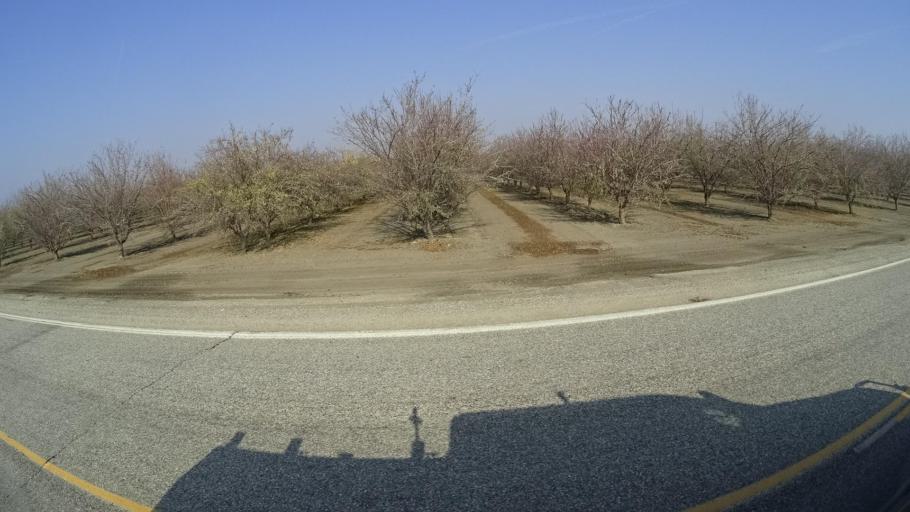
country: US
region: California
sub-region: Kern County
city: Buttonwillow
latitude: 35.3548
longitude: -119.3781
